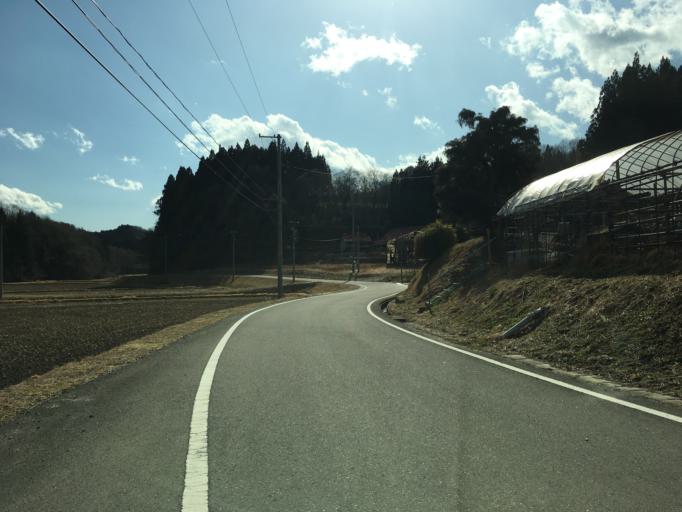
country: JP
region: Fukushima
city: Ishikawa
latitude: 37.2471
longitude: 140.5967
